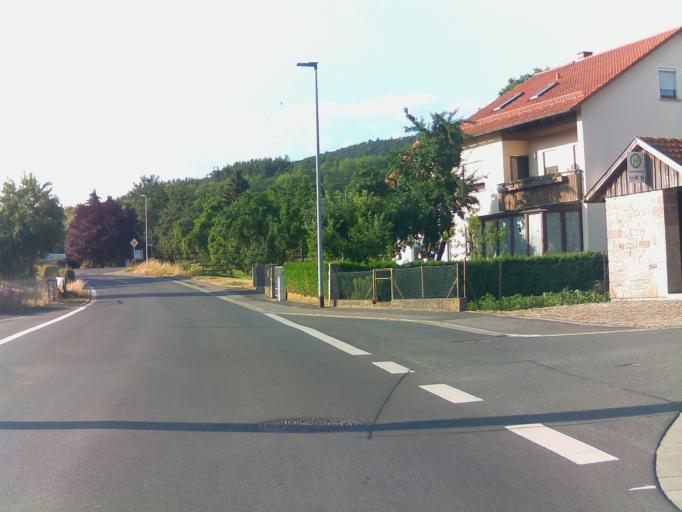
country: DE
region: Bavaria
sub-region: Regierungsbezirk Unterfranken
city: Bastheim
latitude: 50.4251
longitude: 10.1801
